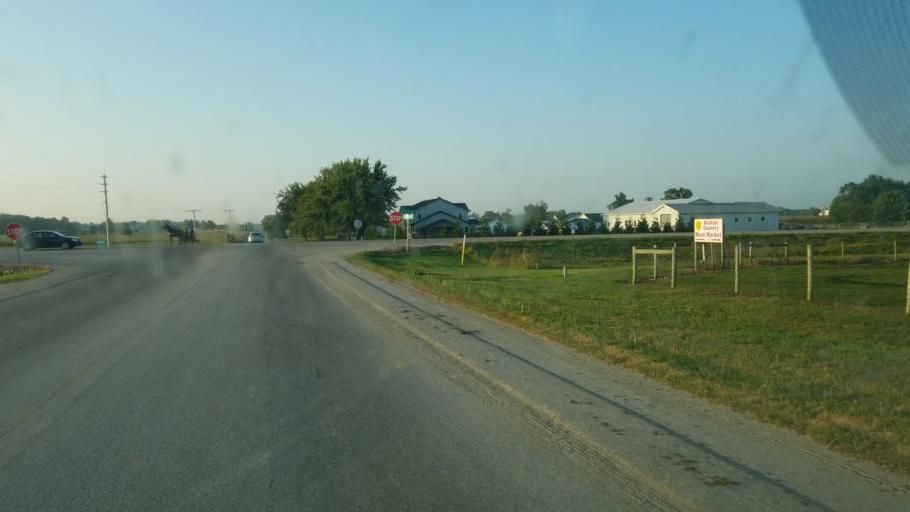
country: US
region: Indiana
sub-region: LaGrange County
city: Topeka
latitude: 41.6410
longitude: -85.5413
